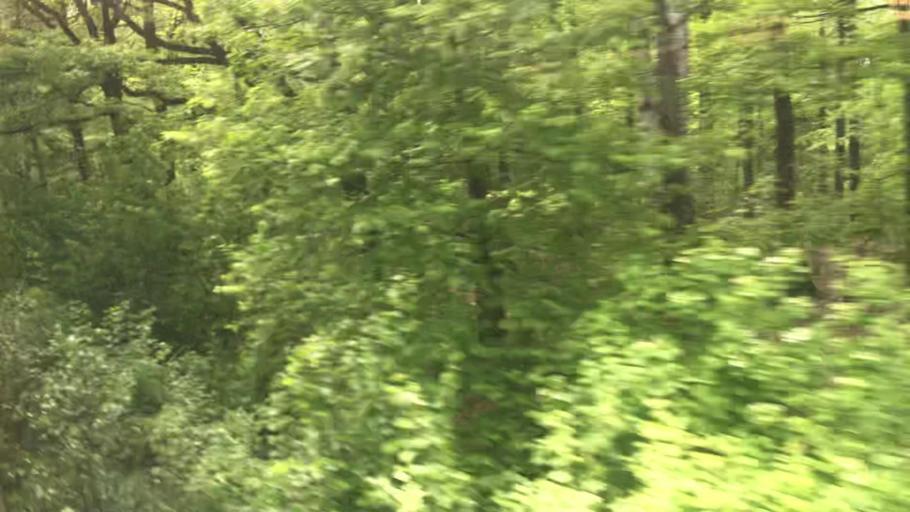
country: PL
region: Lower Silesian Voivodeship
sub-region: Powiat swidnicki
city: Swiebodzice
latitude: 50.8280
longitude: 16.3170
